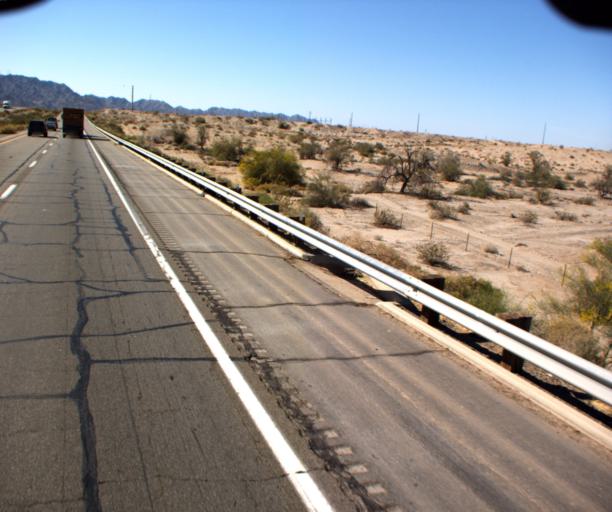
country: US
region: Arizona
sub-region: Yuma County
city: Wellton
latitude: 32.6604
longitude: -114.2558
